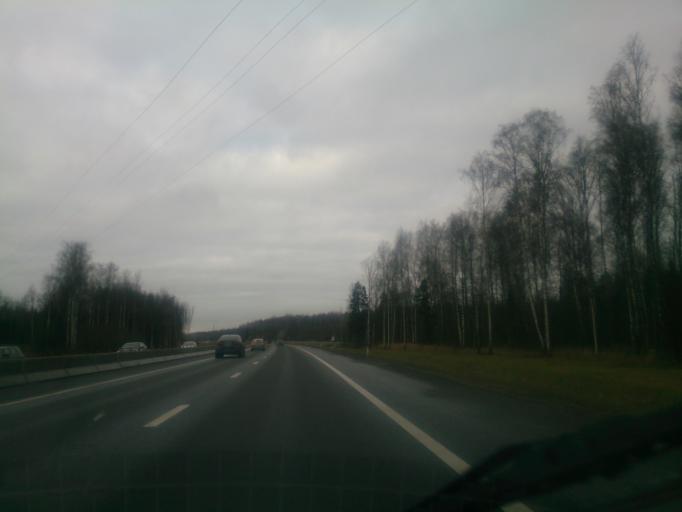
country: RU
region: Leningrad
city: Ul'yanovka
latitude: 59.5939
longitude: 30.7781
